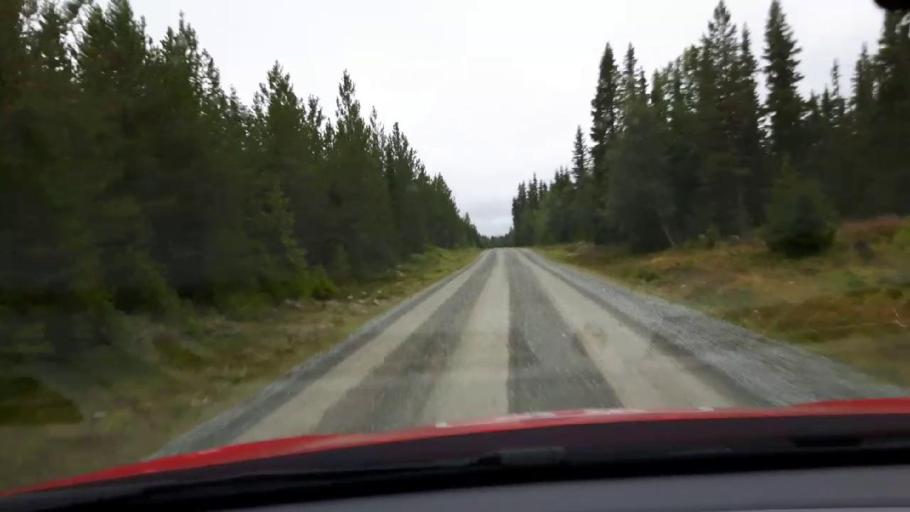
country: SE
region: Jaemtland
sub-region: Bergs Kommun
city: Hoverberg
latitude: 62.8687
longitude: 13.9568
